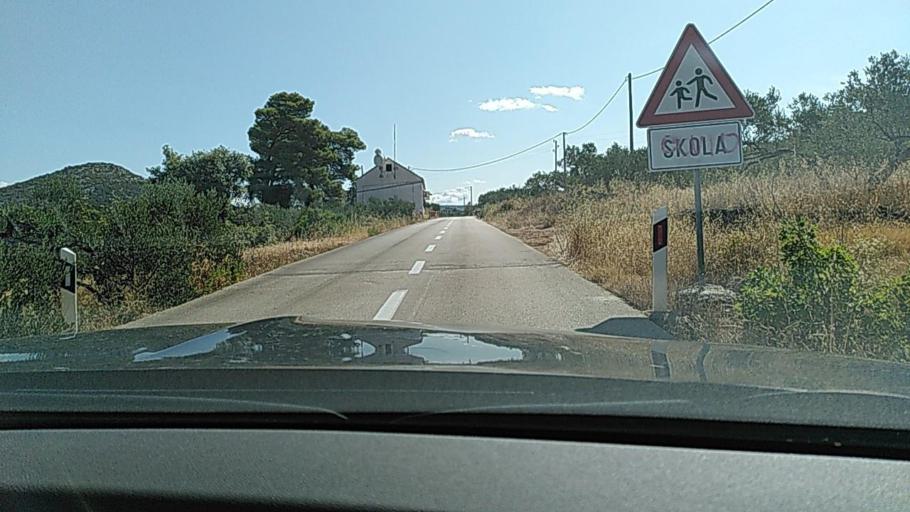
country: HR
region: Splitsko-Dalmatinska
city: Jelsa
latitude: 43.1444
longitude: 16.8394
